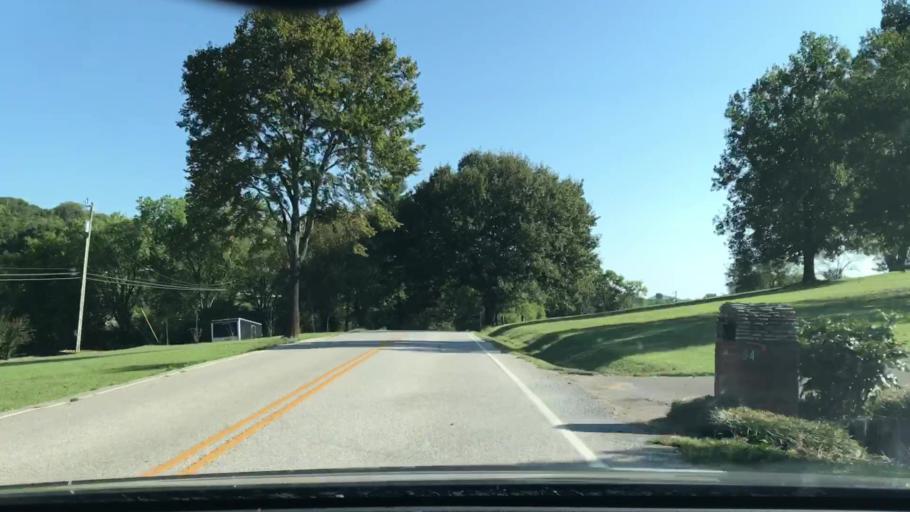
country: US
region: Tennessee
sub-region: Smith County
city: Carthage
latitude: 36.2751
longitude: -85.9525
